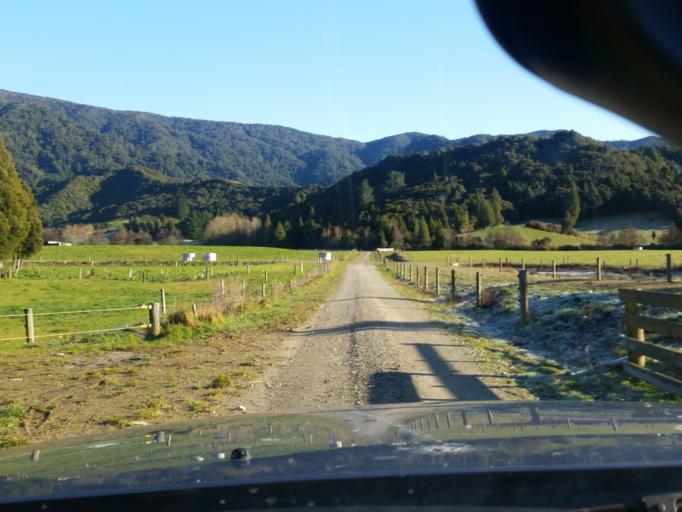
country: NZ
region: Tasman
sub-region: Tasman District
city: Takaka
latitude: -40.7452
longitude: 172.5656
